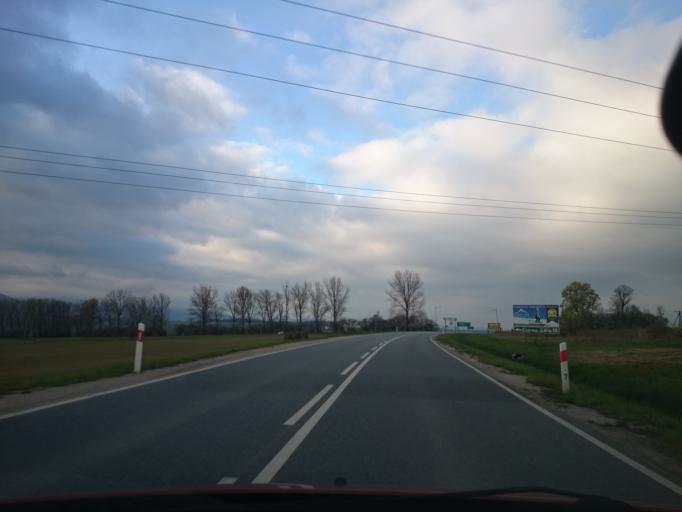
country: PL
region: Lower Silesian Voivodeship
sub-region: Powiat klodzki
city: Bystrzyca Klodzka
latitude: 50.2935
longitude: 16.6631
